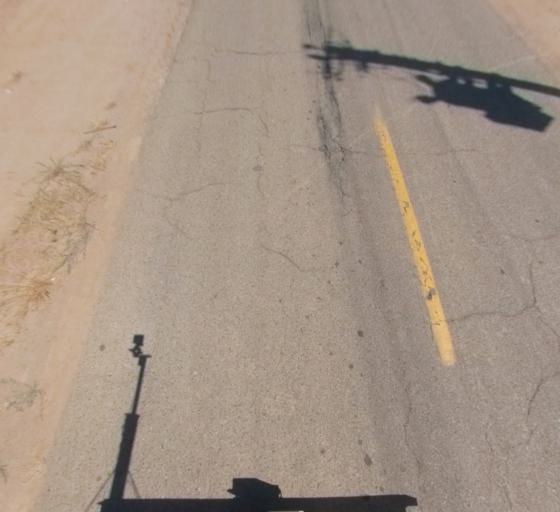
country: US
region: California
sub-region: Madera County
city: Parksdale
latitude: 36.9077
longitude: -119.9394
